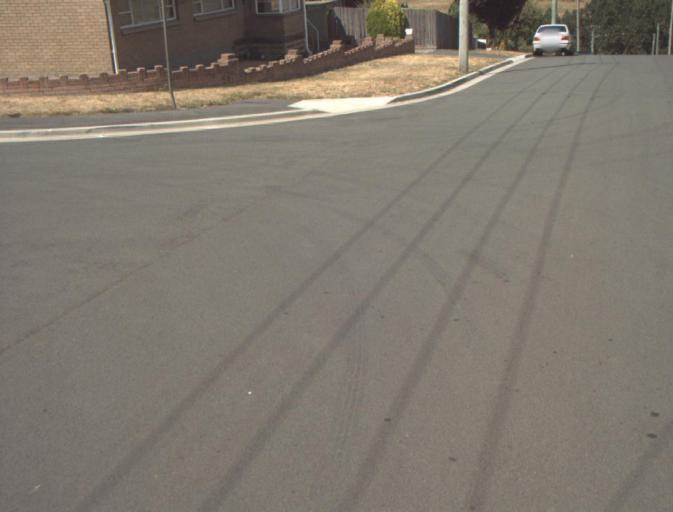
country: AU
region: Tasmania
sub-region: Launceston
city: Newnham
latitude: -41.4113
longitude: 147.1489
